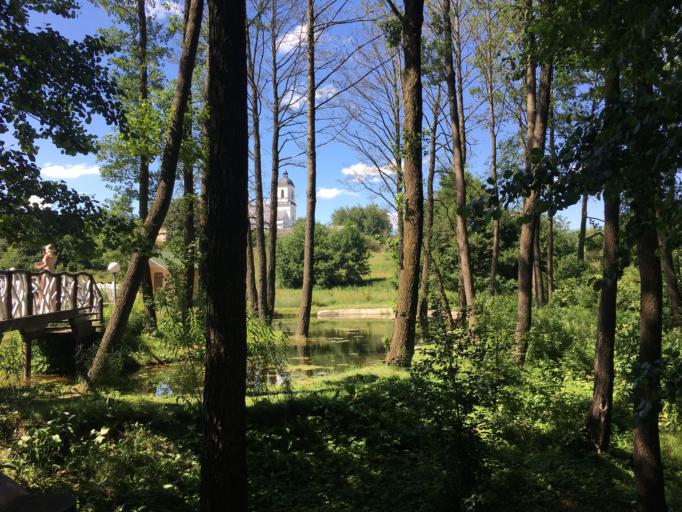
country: BY
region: Grodnenskaya
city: Indura
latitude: 53.5628
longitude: 23.8720
